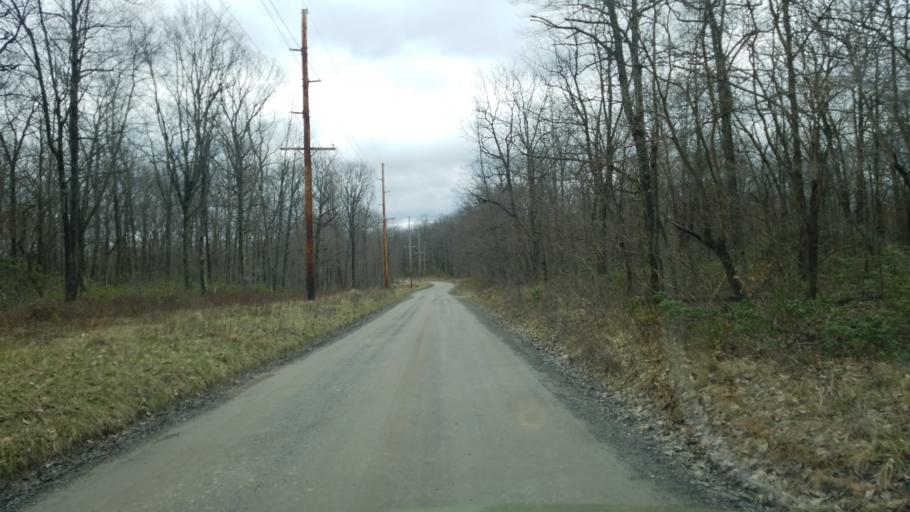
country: US
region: Pennsylvania
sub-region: Clearfield County
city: Shiloh
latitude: 41.1724
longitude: -78.2969
